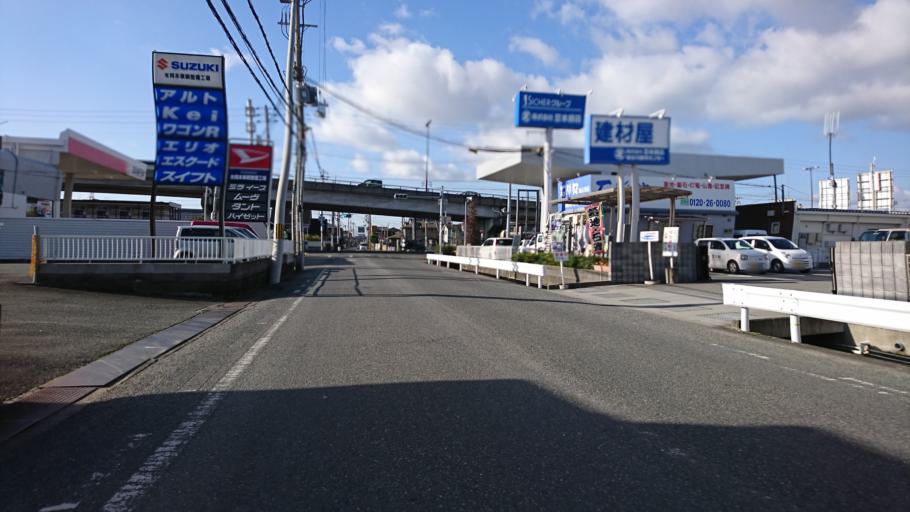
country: JP
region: Hyogo
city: Kakogawacho-honmachi
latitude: 34.7568
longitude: 134.8237
